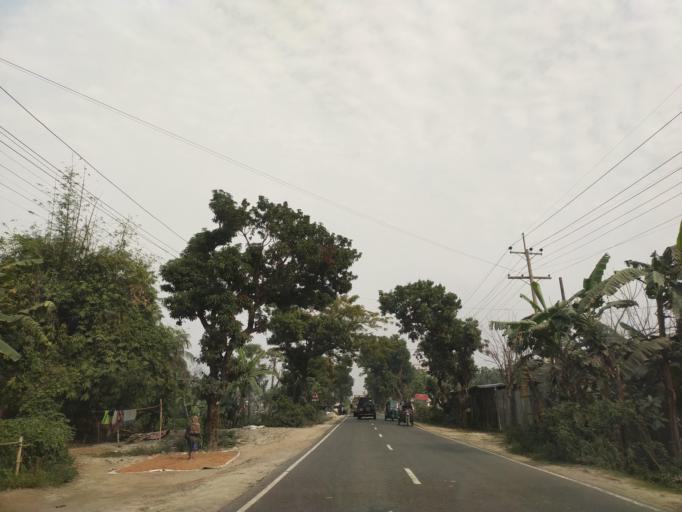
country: BD
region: Dhaka
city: Narsingdi
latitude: 23.9864
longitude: 90.7353
